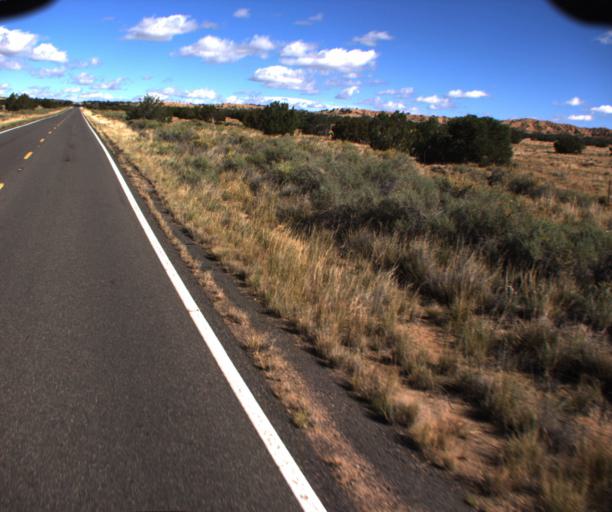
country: US
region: Arizona
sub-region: Apache County
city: Saint Johns
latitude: 34.8064
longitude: -109.2378
